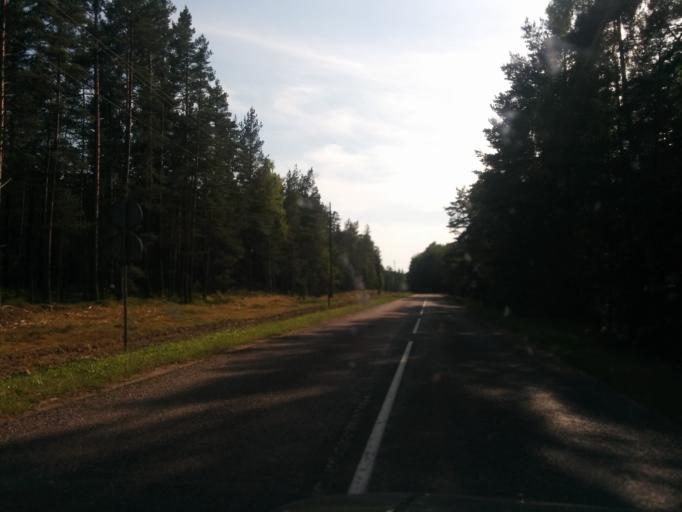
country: LV
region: Dundaga
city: Dundaga
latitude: 57.6721
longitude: 22.3242
